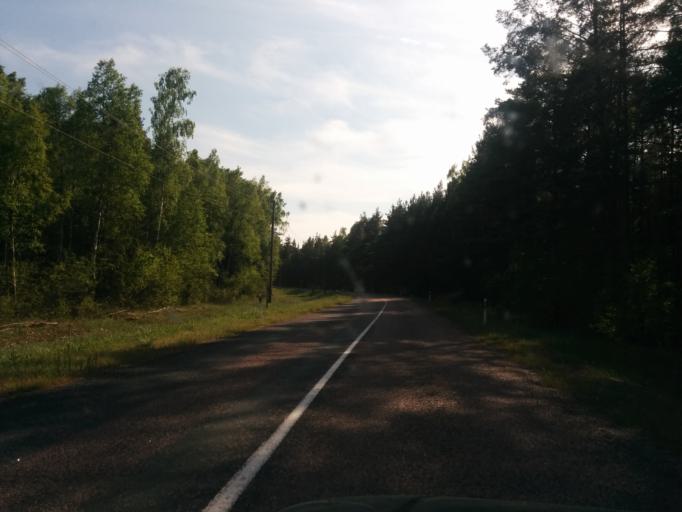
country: LV
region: Dundaga
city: Dundaga
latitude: 57.6539
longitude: 22.2707
